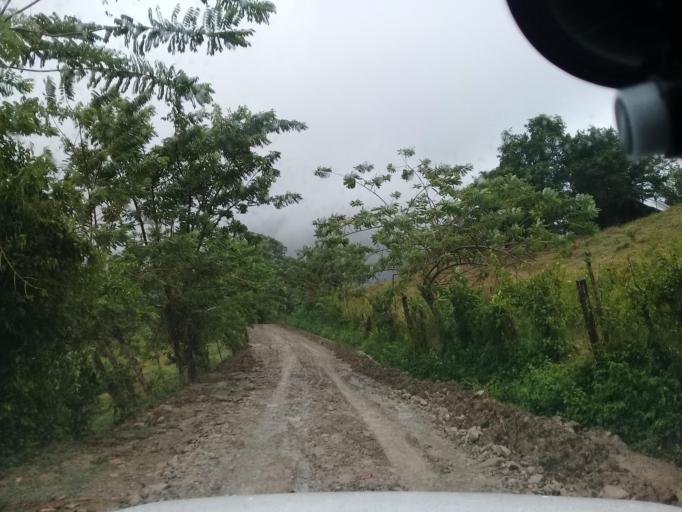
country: MX
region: Veracruz
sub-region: Chalma
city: San Pedro Coyutla
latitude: 21.2299
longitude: -98.4483
